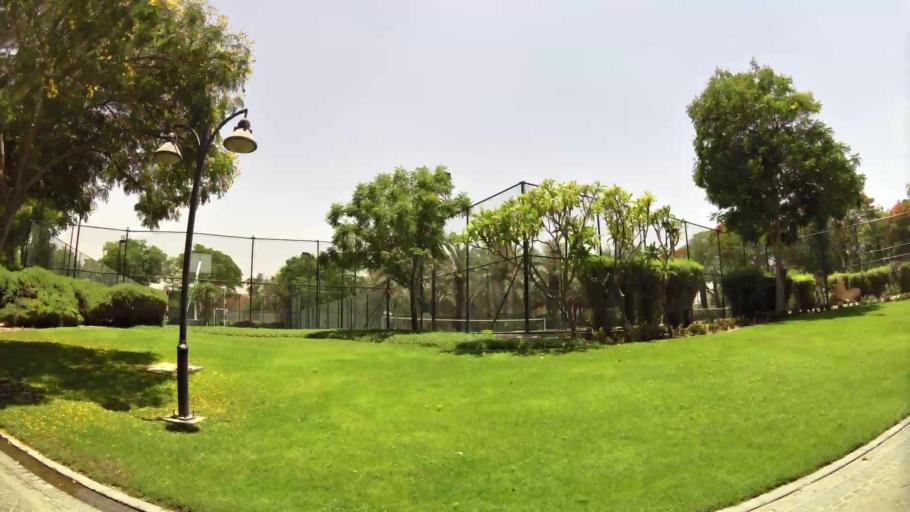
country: AE
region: Dubai
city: Dubai
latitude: 25.0044
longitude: 55.1624
